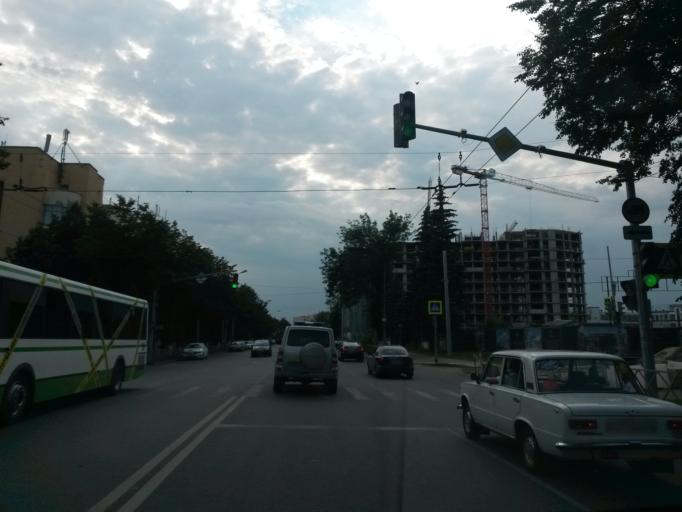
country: RU
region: Jaroslavl
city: Yaroslavl
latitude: 57.6267
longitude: 39.8539
